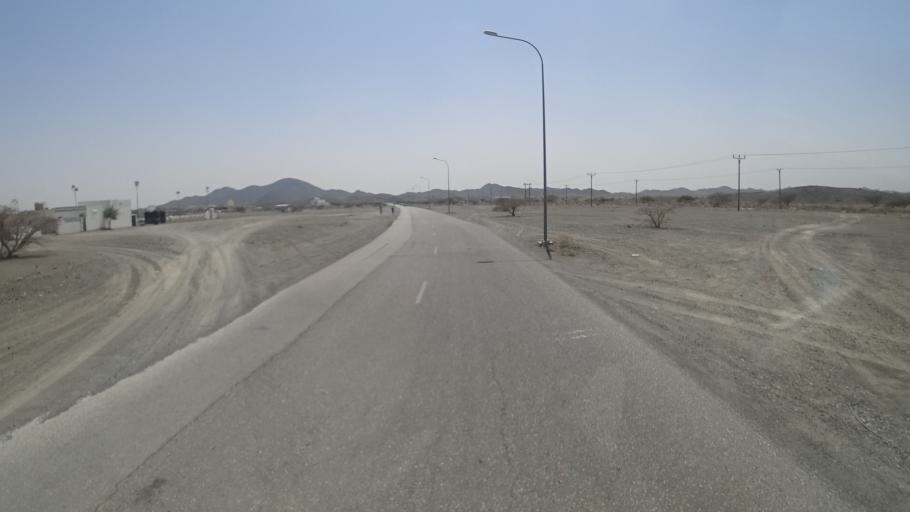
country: OM
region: Ash Sharqiyah
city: Ibra'
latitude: 22.6599
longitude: 58.5263
